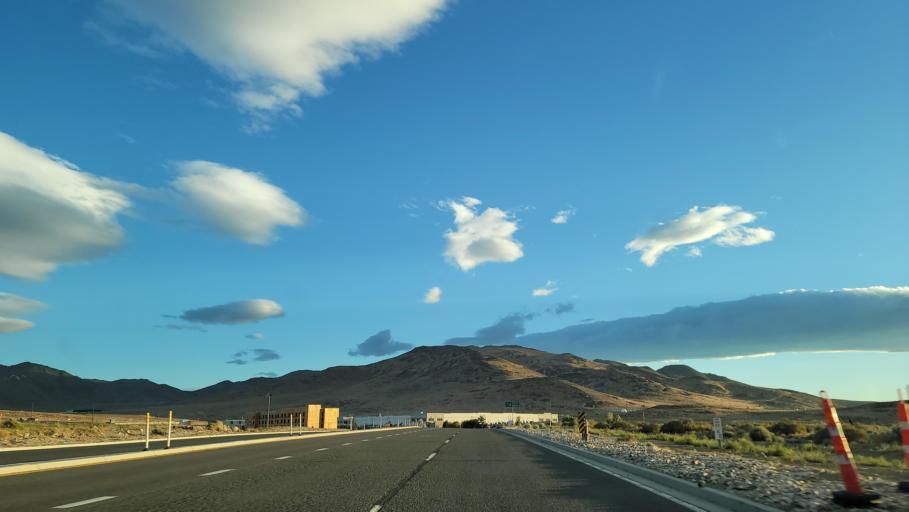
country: US
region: Nevada
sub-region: Lyon County
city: Stagecoach
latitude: 39.5603
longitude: -119.4869
